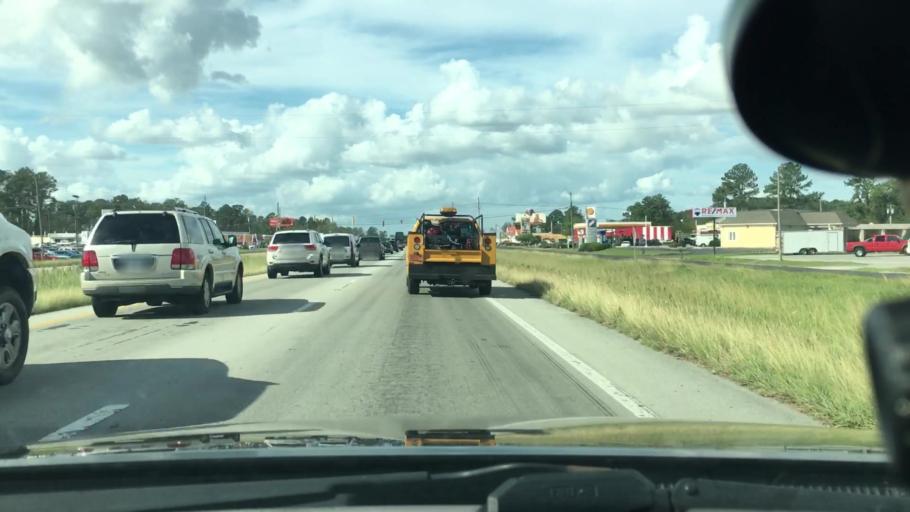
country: US
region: North Carolina
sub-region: Craven County
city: James City
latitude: 35.0732
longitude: -77.0269
